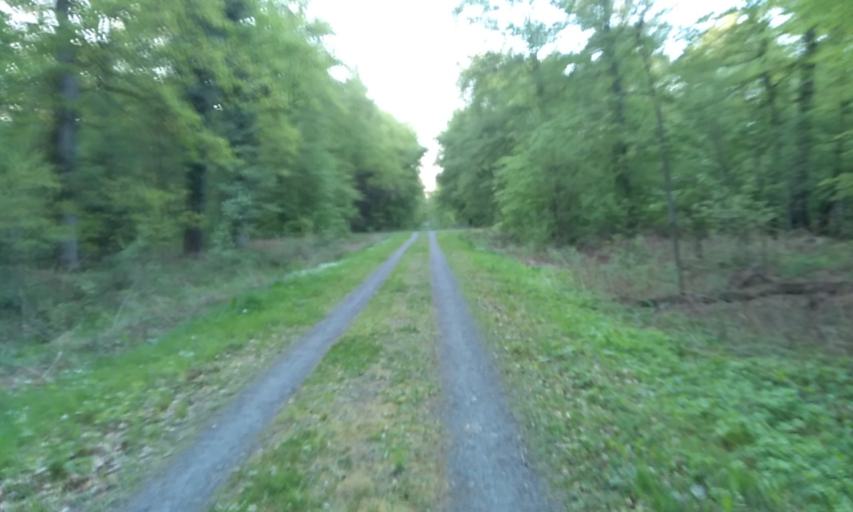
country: DE
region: Lower Saxony
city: Harsefeld
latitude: 53.4172
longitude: 9.5022
